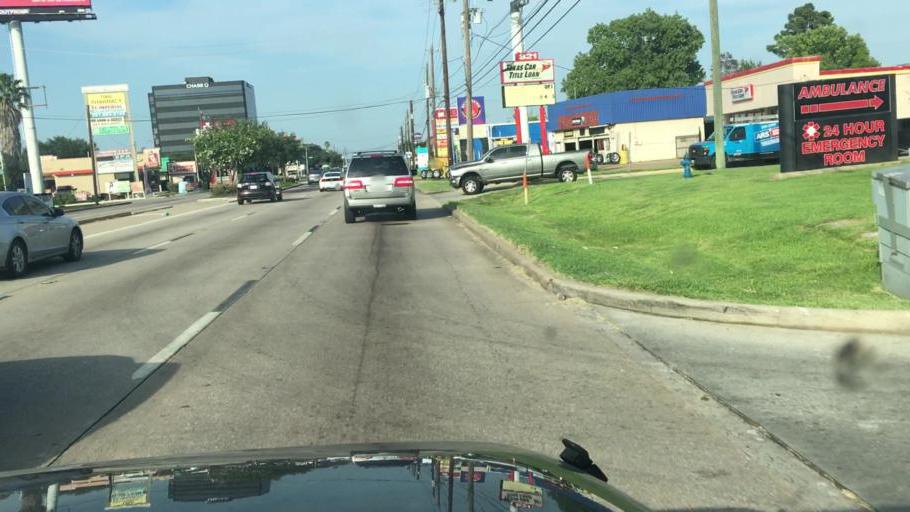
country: US
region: Texas
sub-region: Harris County
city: Spring
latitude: 30.0172
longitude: -95.4424
